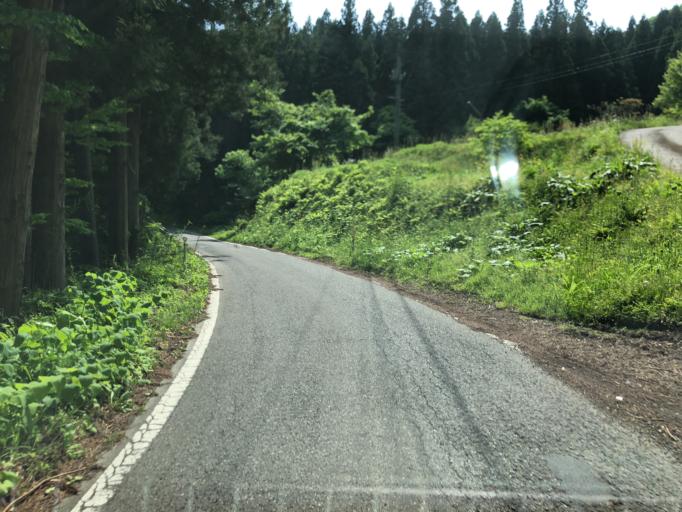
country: JP
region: Fukushima
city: Ishikawa
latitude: 37.0458
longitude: 140.5723
